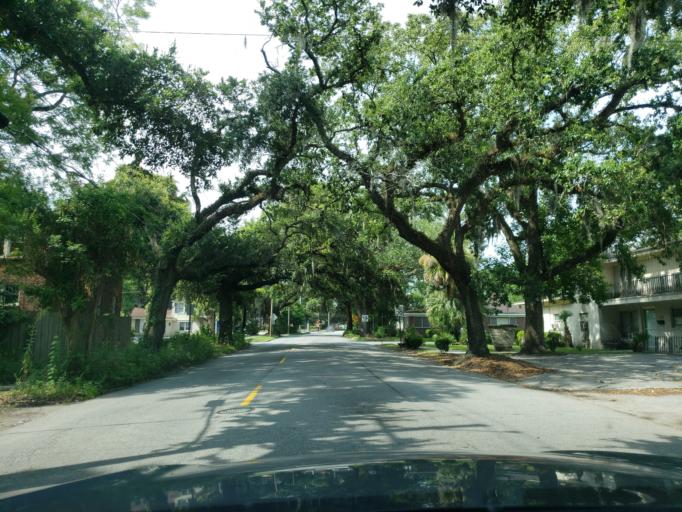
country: US
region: Georgia
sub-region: Chatham County
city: Thunderbolt
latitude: 32.0426
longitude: -81.0873
